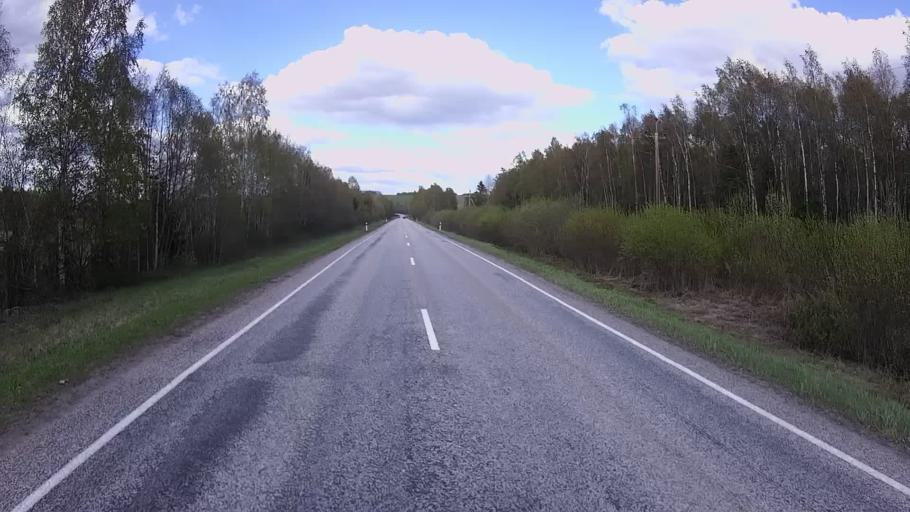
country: EE
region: Jogevamaa
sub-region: Jogeva linn
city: Jogeva
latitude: 58.7710
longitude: 26.4570
